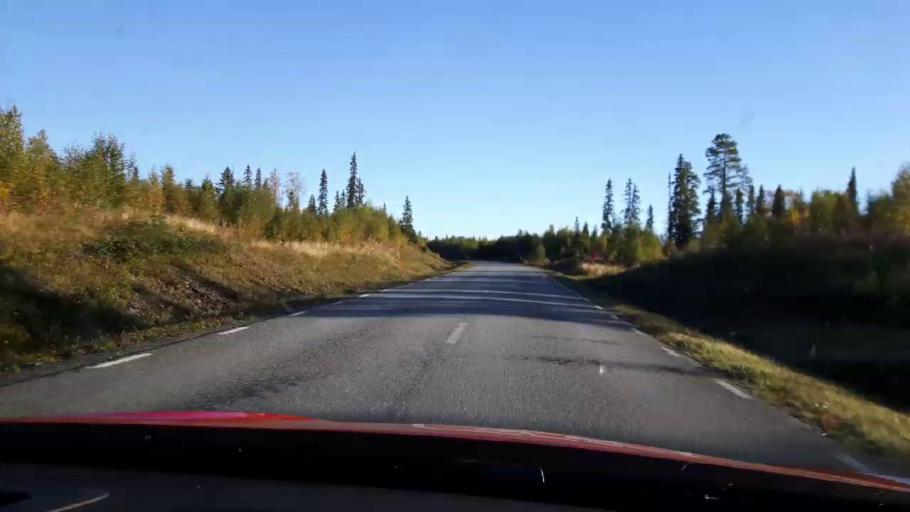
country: SE
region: Jaemtland
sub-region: OEstersunds Kommun
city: Lit
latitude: 63.7816
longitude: 14.7064
